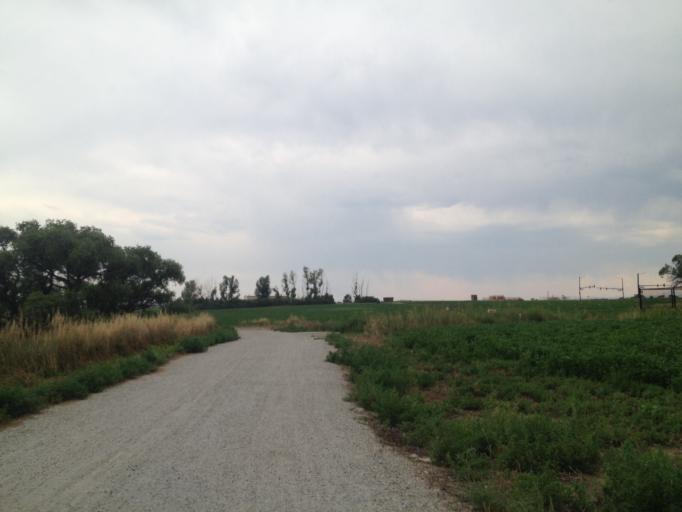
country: US
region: Colorado
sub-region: Boulder County
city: Erie
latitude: 40.0174
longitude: -105.0526
